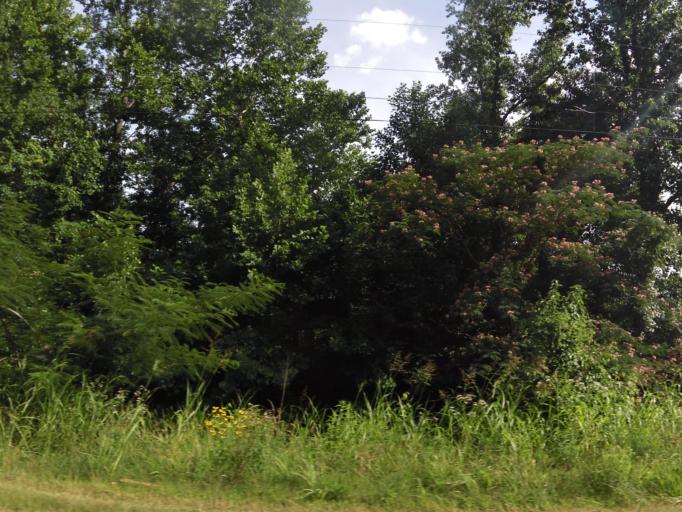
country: US
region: Tennessee
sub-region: Carroll County
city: Bruceton
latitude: 36.0351
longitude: -88.1981
